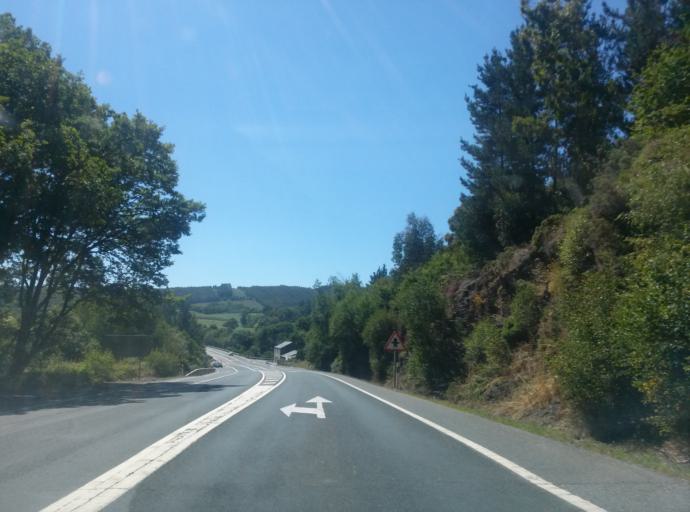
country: ES
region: Galicia
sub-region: Provincia de Lugo
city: Pol
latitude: 43.1702
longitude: -7.3677
